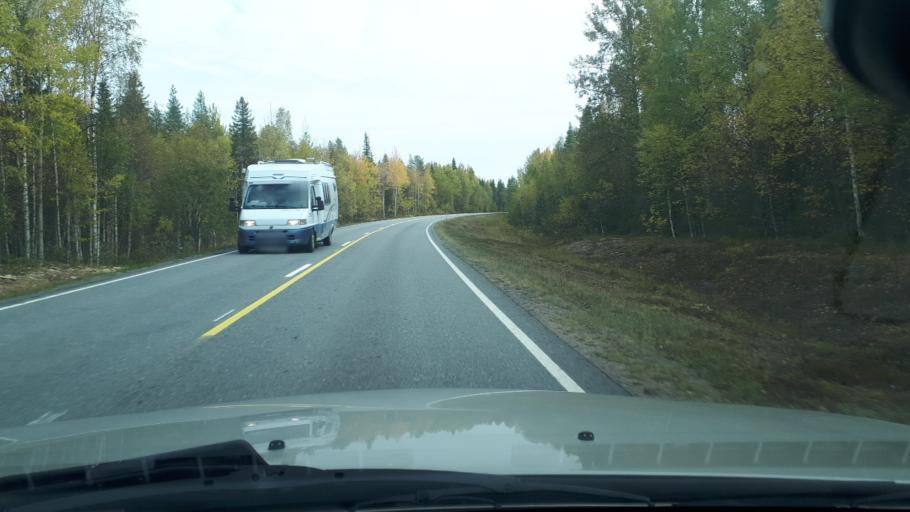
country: FI
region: Lapland
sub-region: Rovaniemi
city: Ranua
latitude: 66.0086
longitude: 26.2801
